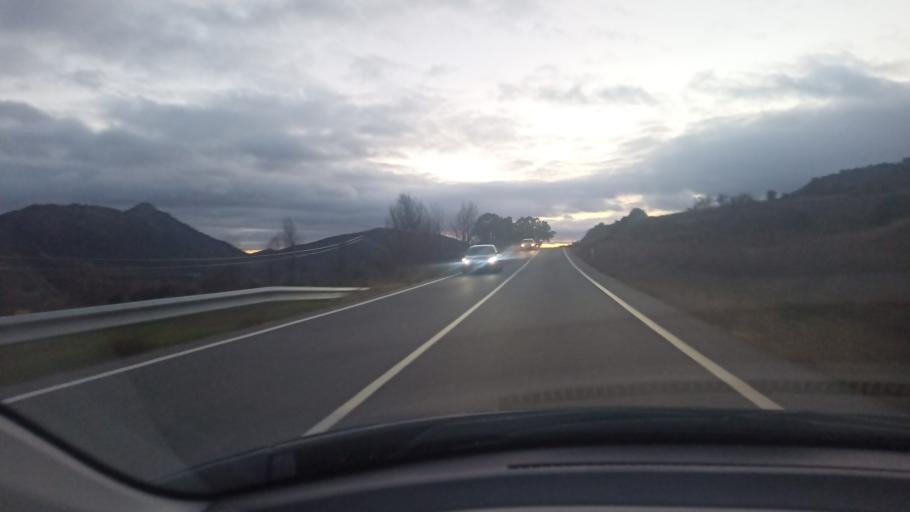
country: ES
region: Madrid
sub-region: Provincia de Madrid
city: Robledo de Chavela
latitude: 40.4881
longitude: -4.2478
